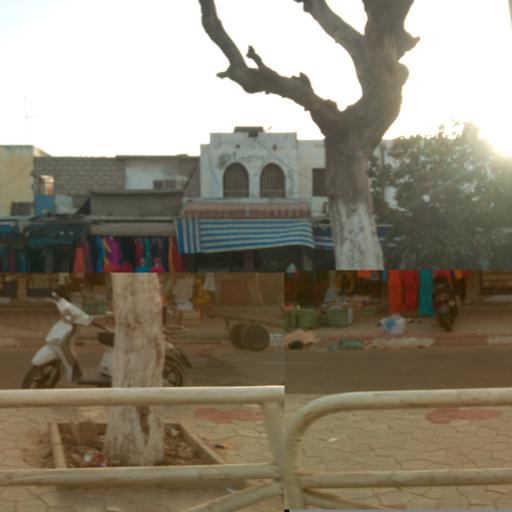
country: SN
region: Dakar
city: Dakar
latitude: 14.6887
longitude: -17.4463
